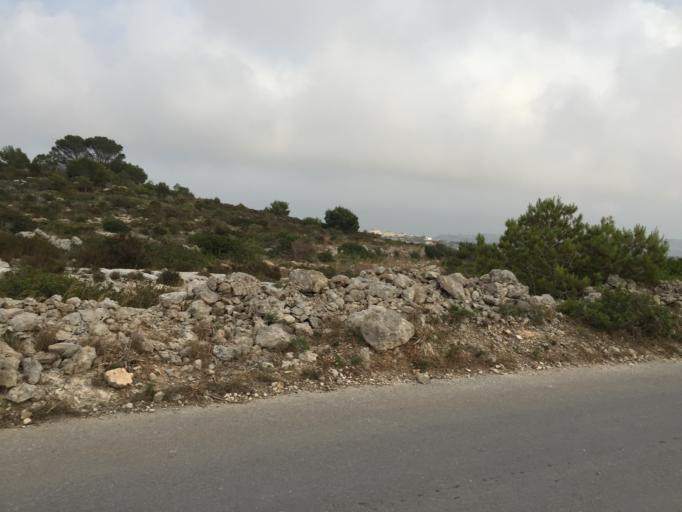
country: MT
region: L-Imgarr
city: Imgarr
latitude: 35.9358
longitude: 14.3903
